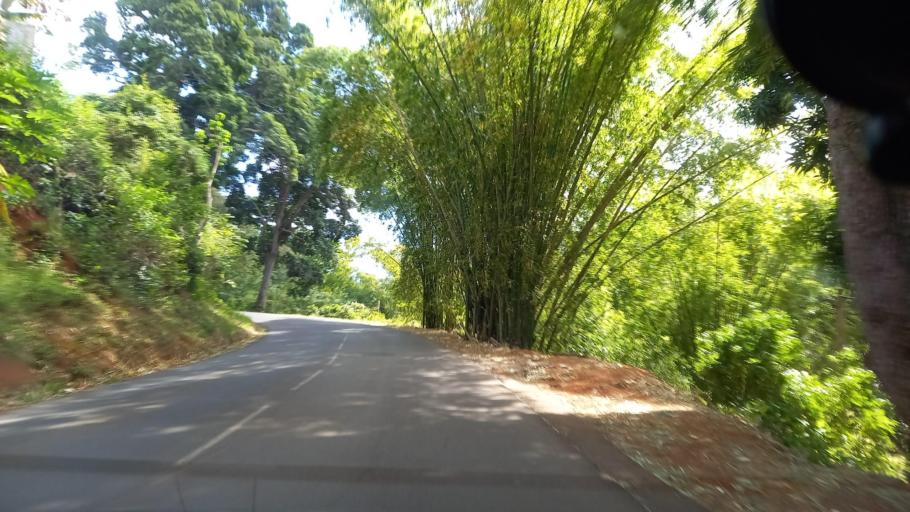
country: YT
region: Mamoudzou
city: Mamoudzou
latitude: -12.7974
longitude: 45.2012
